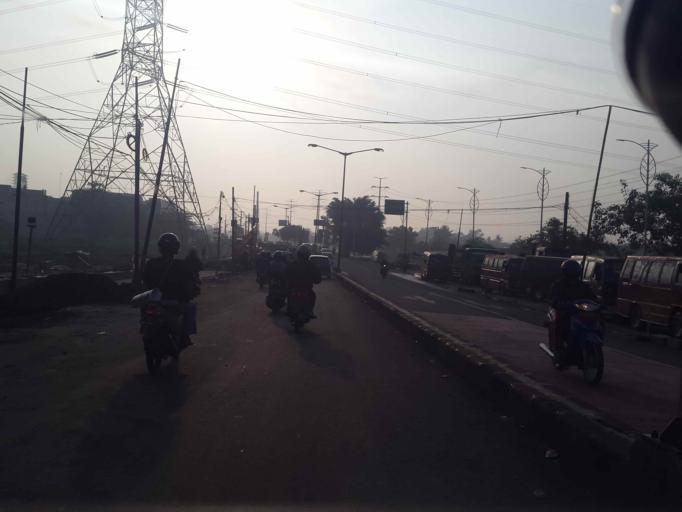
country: ID
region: West Java
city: Bekasi
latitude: -6.2609
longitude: 107.0190
